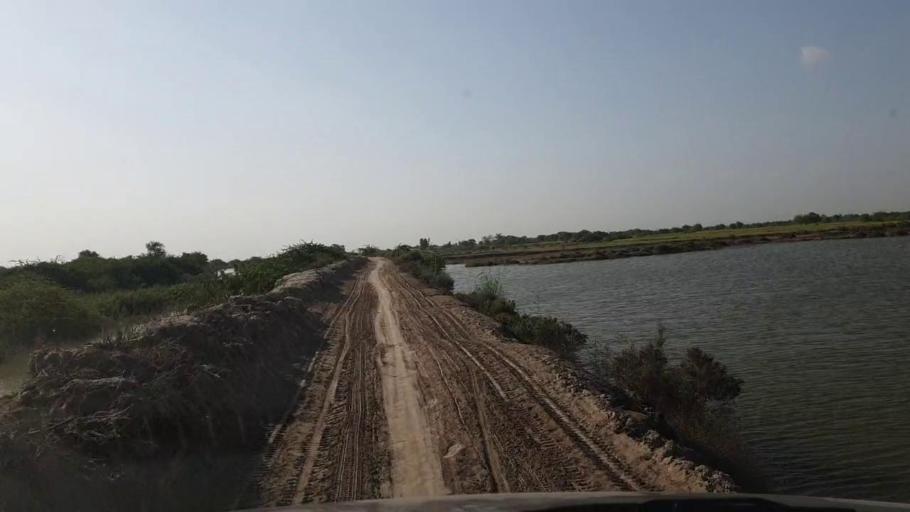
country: PK
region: Sindh
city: Kadhan
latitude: 24.6232
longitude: 69.0729
